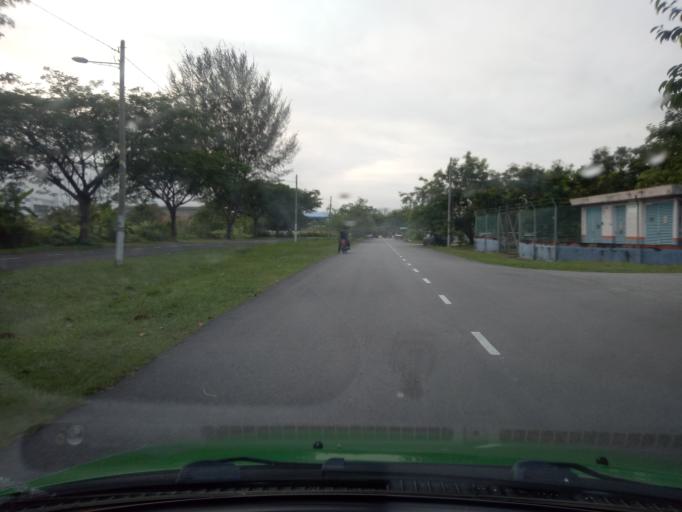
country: MY
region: Selangor
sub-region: Hulu Langat
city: Semenyih
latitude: 2.9304
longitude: 101.8643
